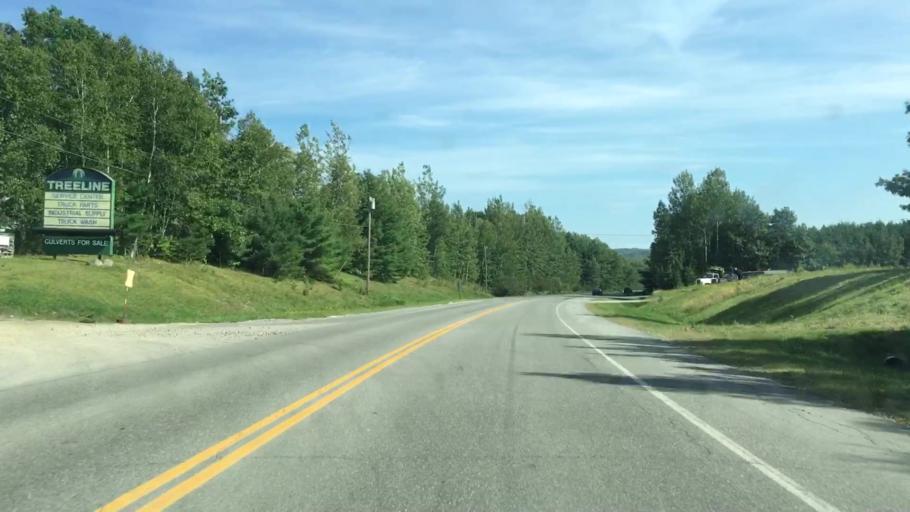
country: US
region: Maine
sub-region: Penobscot County
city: Lincoln
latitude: 45.3693
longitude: -68.5557
